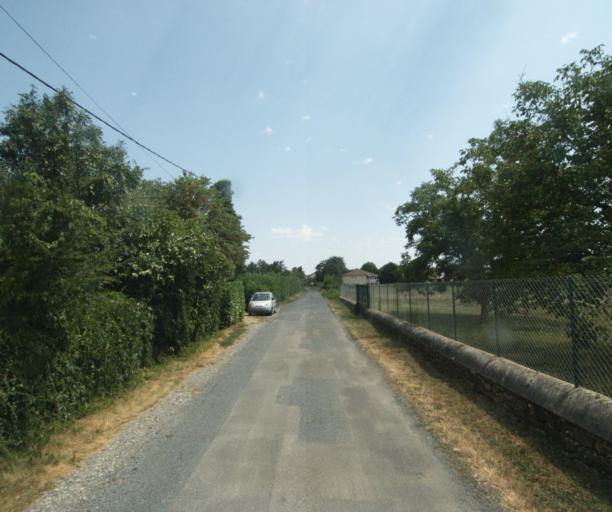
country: FR
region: Rhone-Alpes
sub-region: Departement du Rhone
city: Saint-Germain-Nuelles
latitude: 45.8458
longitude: 4.5997
